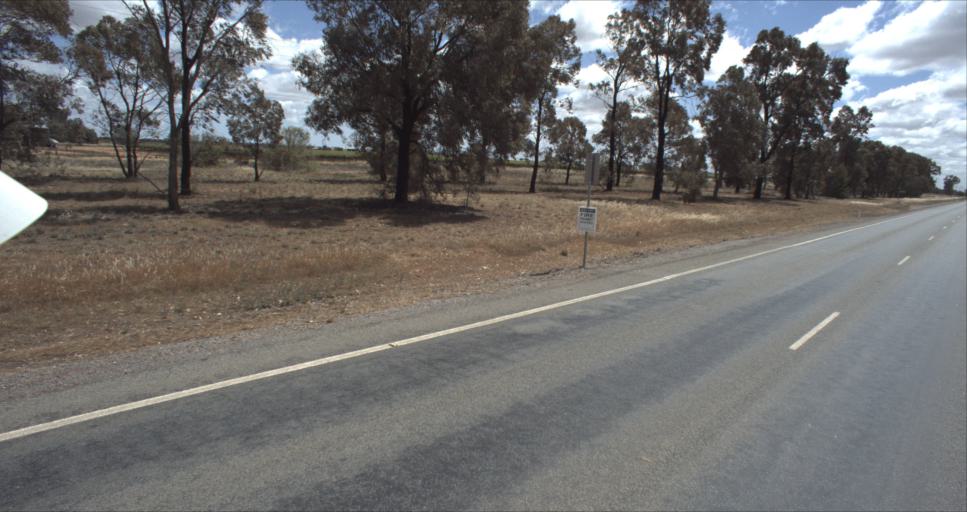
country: AU
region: New South Wales
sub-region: Murrumbidgee Shire
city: Darlington Point
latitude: -34.5090
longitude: 146.1867
